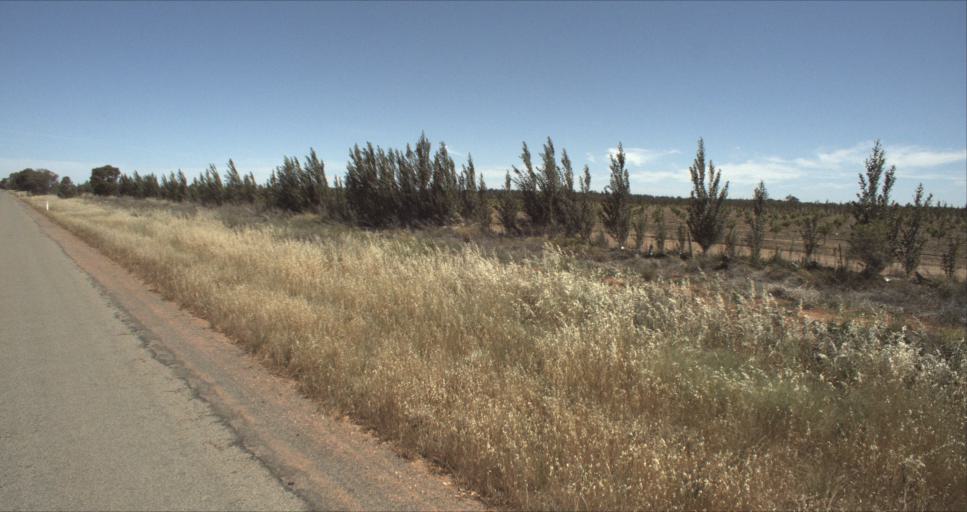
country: AU
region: New South Wales
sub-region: Leeton
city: Leeton
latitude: -34.5138
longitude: 146.3451
